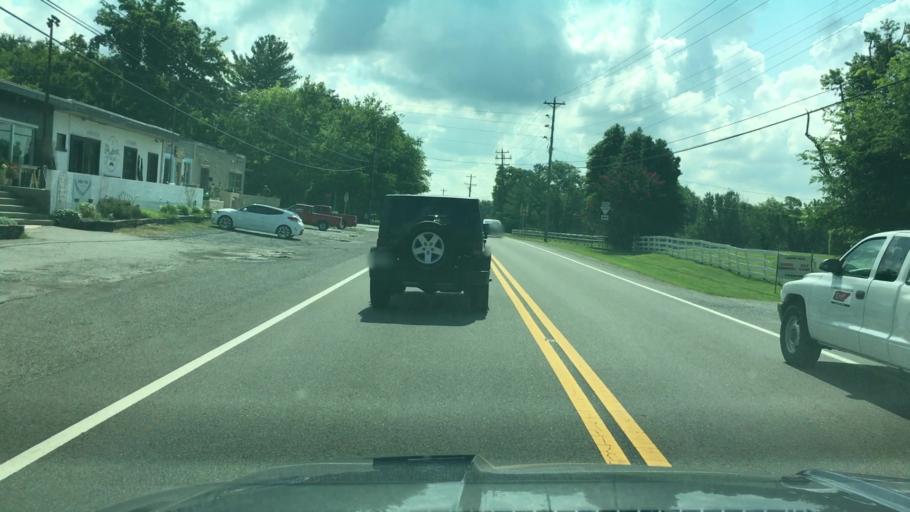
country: US
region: Tennessee
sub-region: Williamson County
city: Nolensville
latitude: 35.8680
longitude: -86.7106
